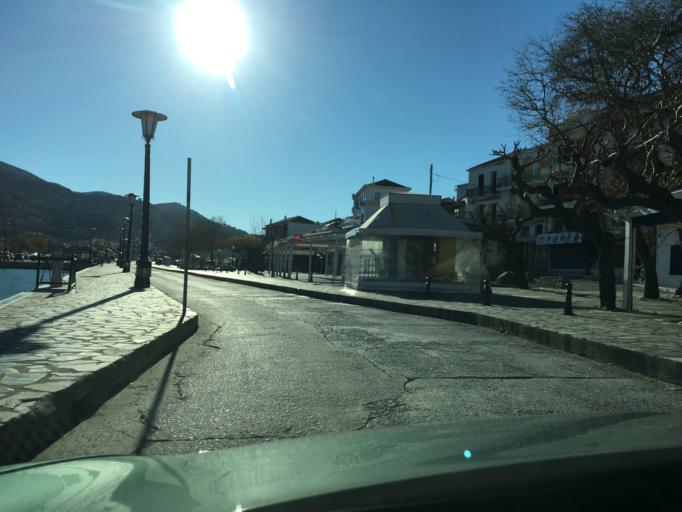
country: GR
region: Thessaly
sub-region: Nomos Magnisias
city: Skopelos
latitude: 39.1222
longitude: 23.7285
